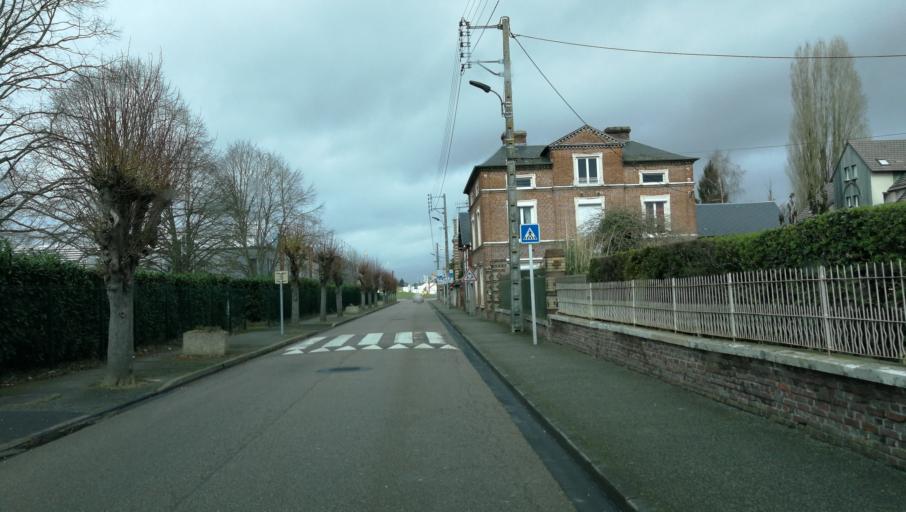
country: FR
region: Haute-Normandie
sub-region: Departement de l'Eure
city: Brionne
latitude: 49.1975
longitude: 0.7167
